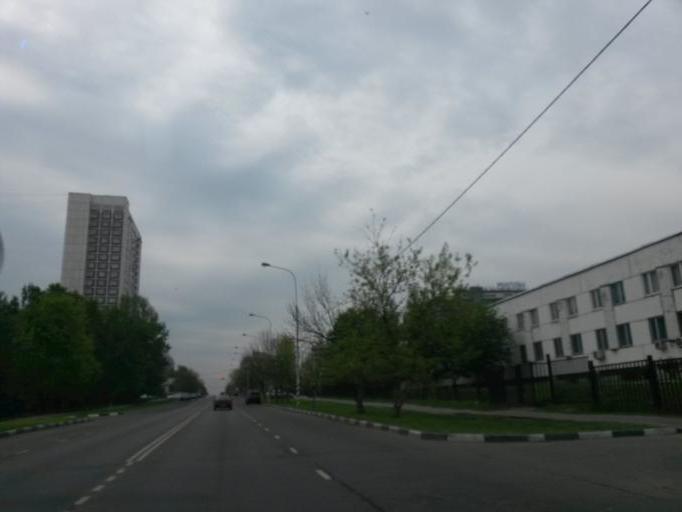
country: RU
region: Moscow
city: Orekhovo-Borisovo
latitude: 55.6225
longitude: 37.7164
